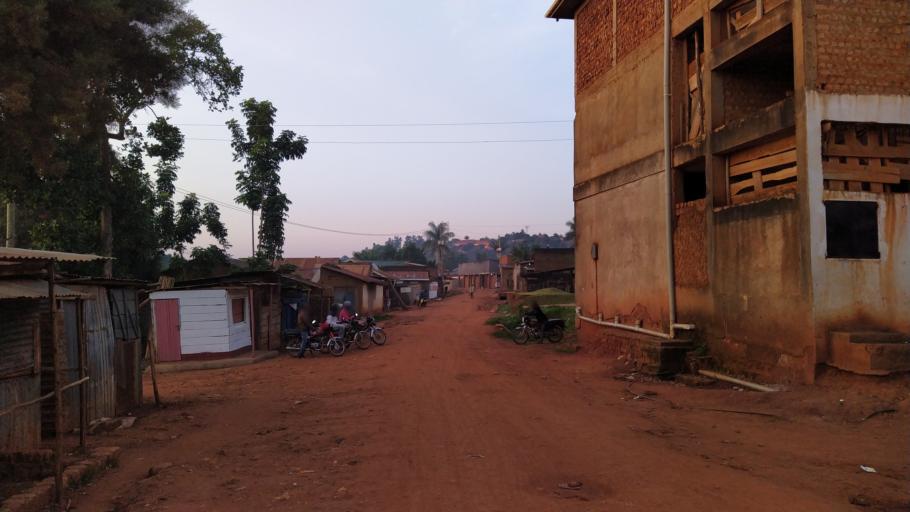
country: UG
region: Central Region
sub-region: Kampala District
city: Kampala
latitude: 0.2738
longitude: 32.5736
